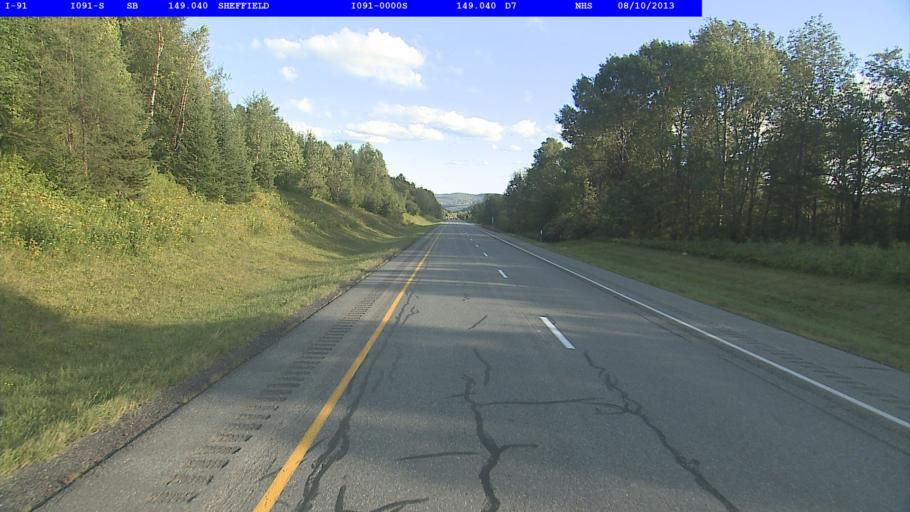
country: US
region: Vermont
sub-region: Caledonia County
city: Lyndonville
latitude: 44.6508
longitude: -72.1344
